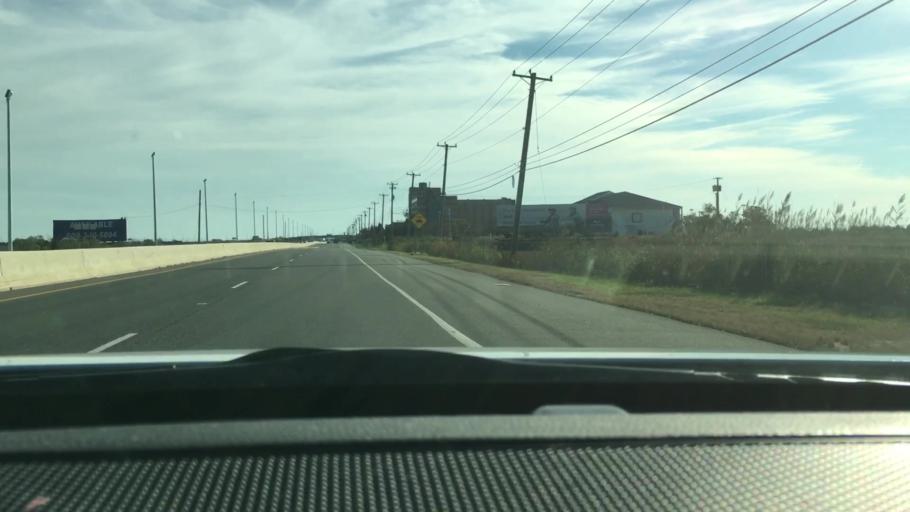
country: US
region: New Jersey
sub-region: Atlantic County
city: Absecon
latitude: 39.4074
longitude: -74.4919
